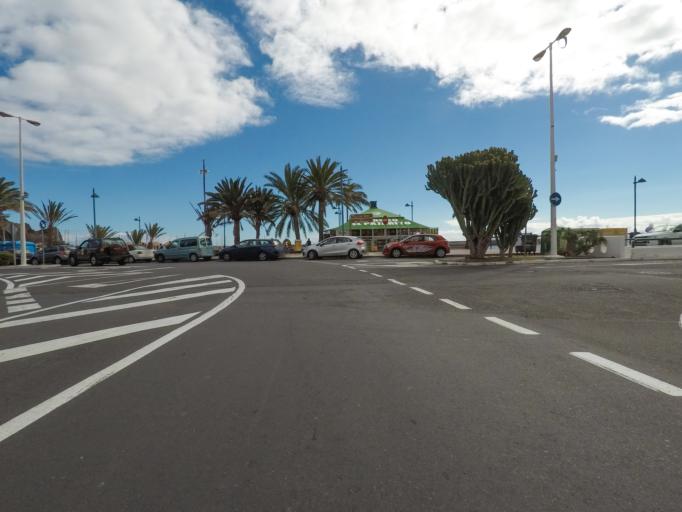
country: ES
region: Canary Islands
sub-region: Provincia de Santa Cruz de Tenerife
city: San Sebastian de la Gomera
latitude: 28.0897
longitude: -17.1116
